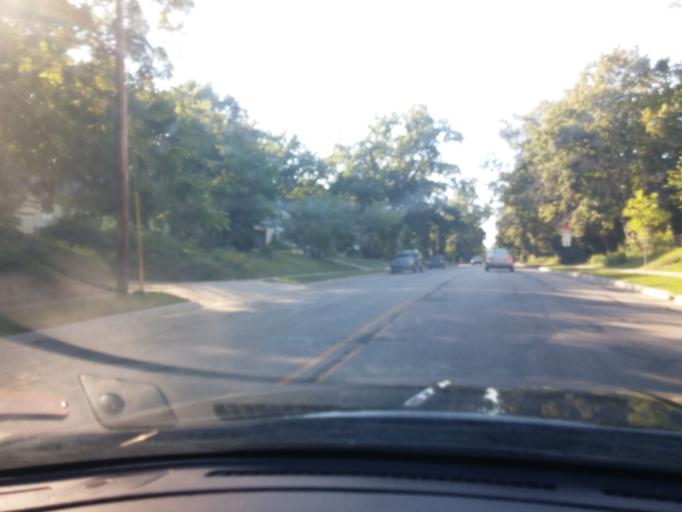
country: US
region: Indiana
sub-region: Tippecanoe County
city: West Lafayette
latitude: 40.4297
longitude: -86.9016
